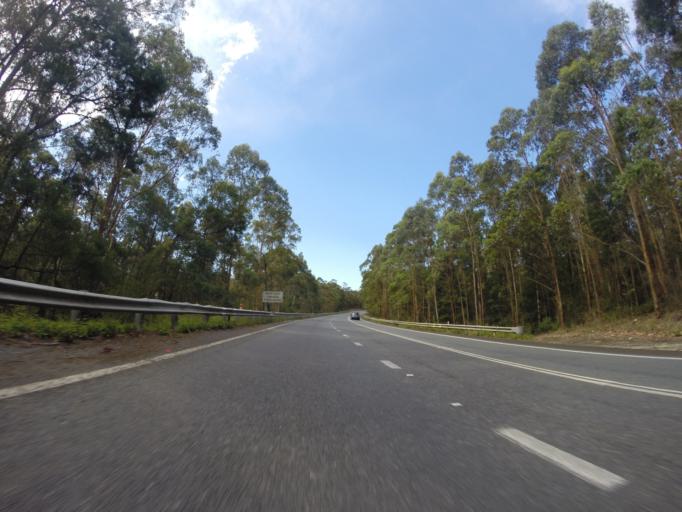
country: AU
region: New South Wales
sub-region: Shoalhaven Shire
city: Falls Creek
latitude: -35.0461
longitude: 150.5771
